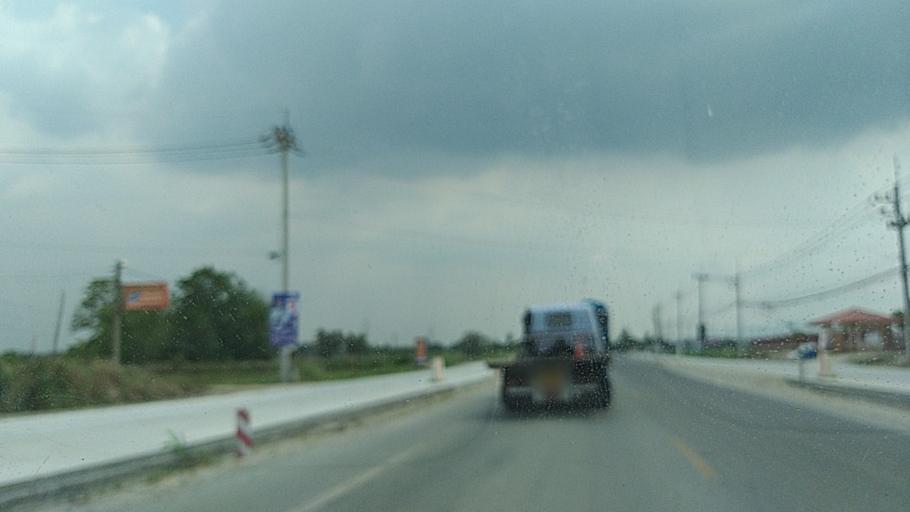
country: TH
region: Chon Buri
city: Ban Bueng
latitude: 13.3293
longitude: 101.1877
